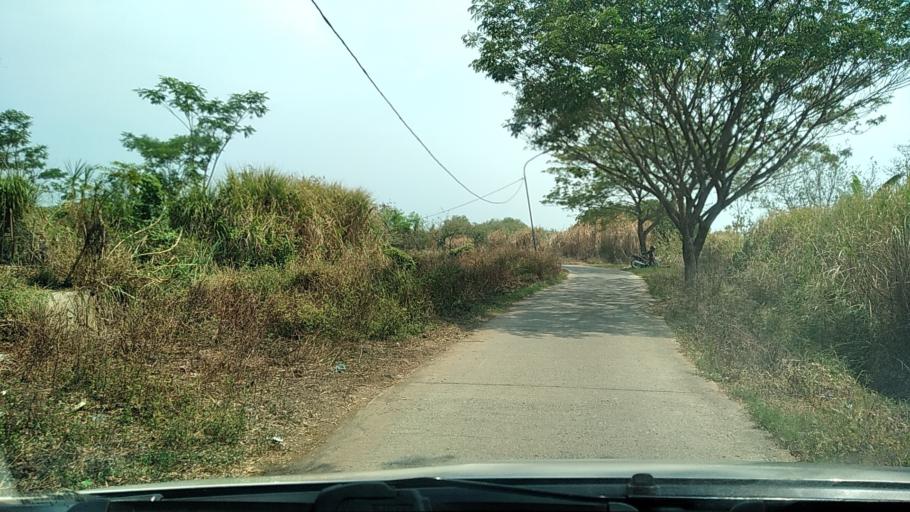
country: ID
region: Central Java
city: Semarang
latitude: -6.9689
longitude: 110.3457
